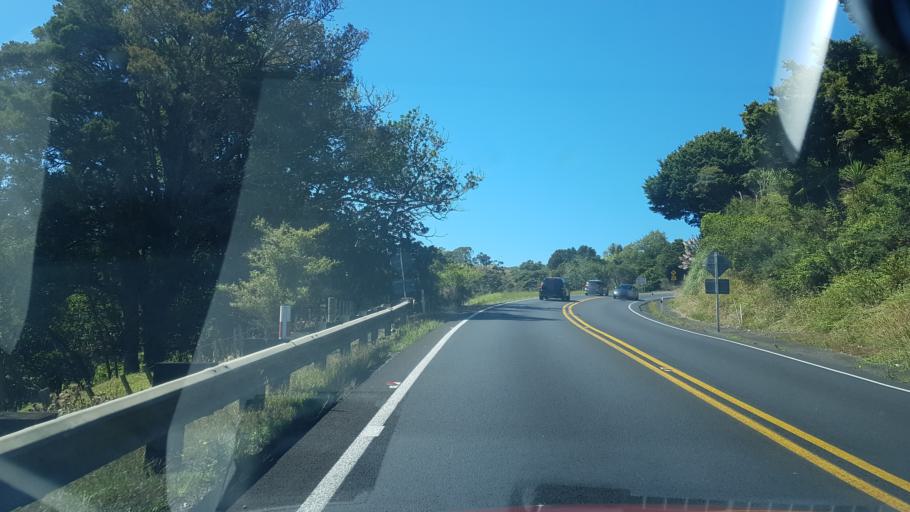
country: NZ
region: Auckland
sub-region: Auckland
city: Warkworth
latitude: -36.4834
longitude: 174.6548
